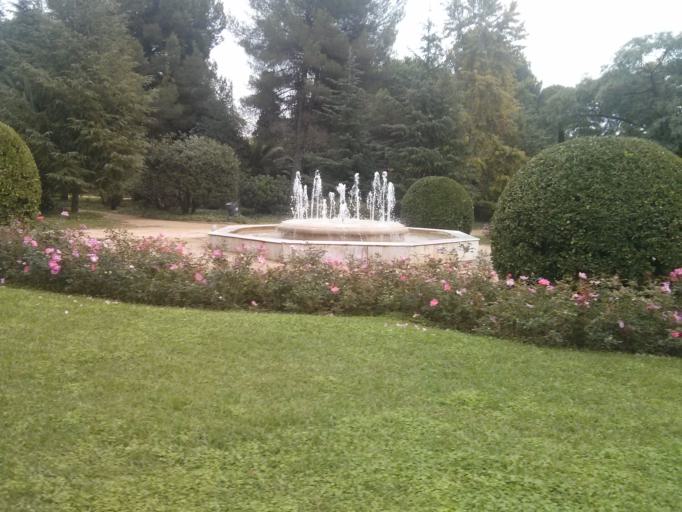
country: ES
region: Catalonia
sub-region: Provincia de Barcelona
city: les Corts
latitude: 41.3874
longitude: 2.1182
